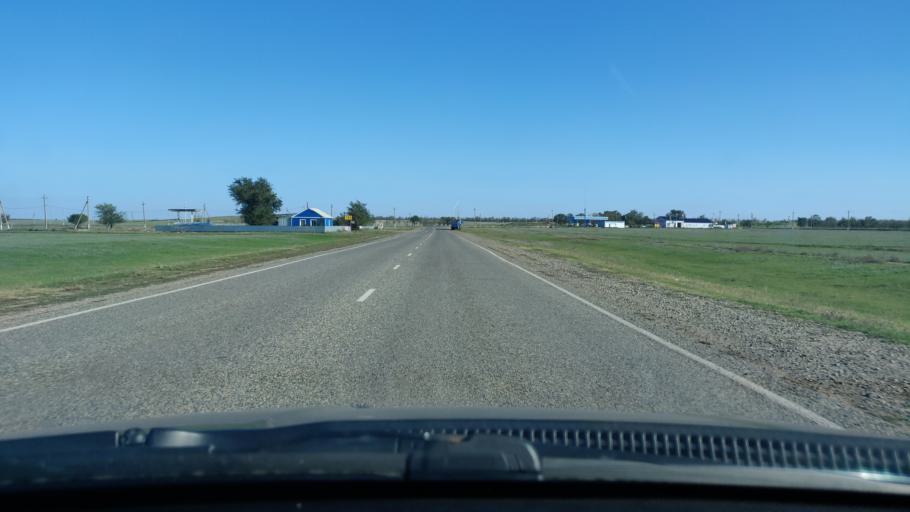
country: RU
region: Stavropol'skiy
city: Letnyaya Stavka
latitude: 45.3740
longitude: 43.6879
